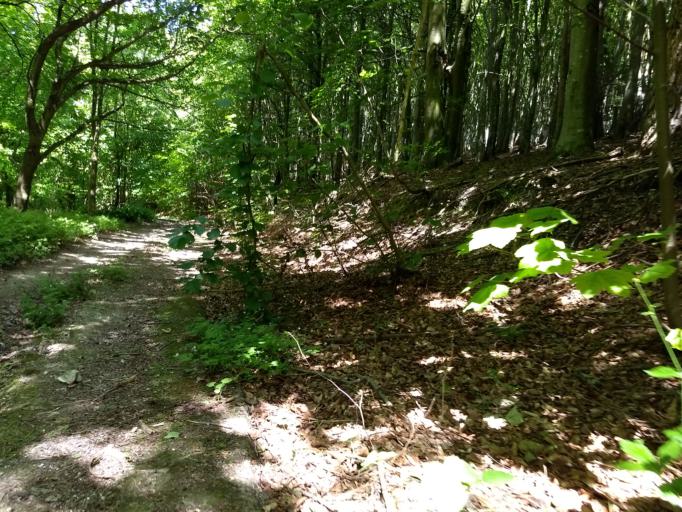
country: GB
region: England
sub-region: Isle of Wight
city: Shalfleet
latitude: 50.6679
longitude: -1.3856
